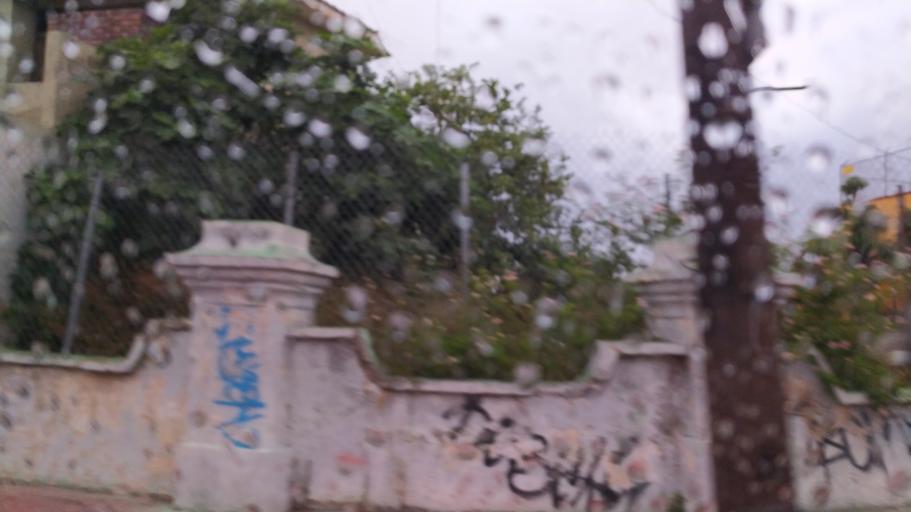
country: MX
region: Jalisco
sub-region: Zapopan
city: Zapopan
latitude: 20.7162
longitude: -103.3597
